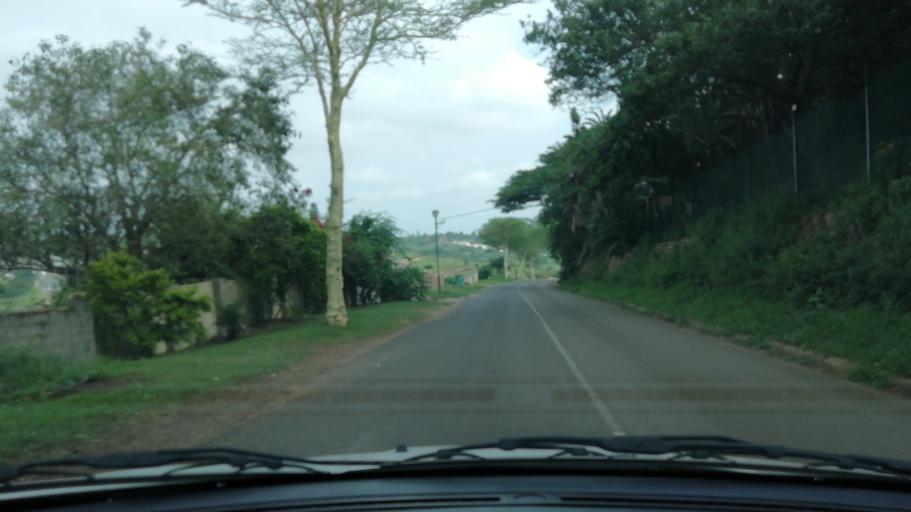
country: ZA
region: KwaZulu-Natal
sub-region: uThungulu District Municipality
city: Empangeni
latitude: -28.7408
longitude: 31.8799
